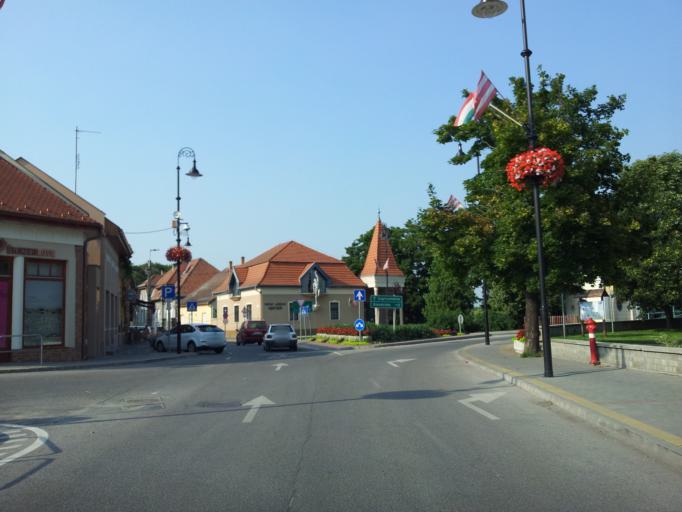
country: HU
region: Pest
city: Rackeve
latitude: 47.1615
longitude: 18.9458
